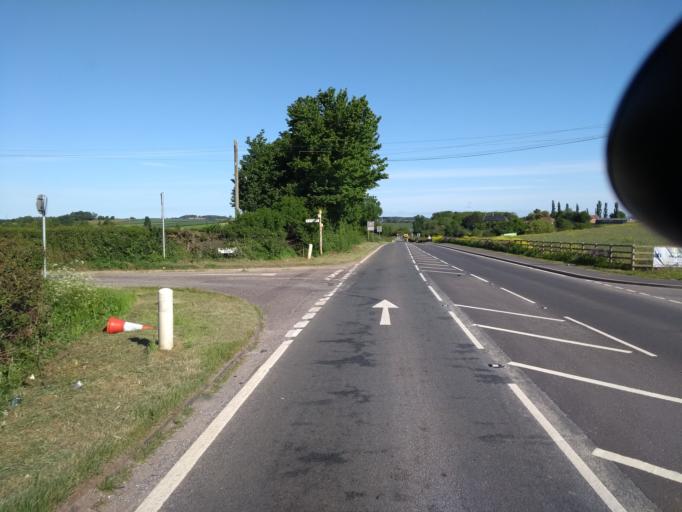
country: GB
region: England
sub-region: Somerset
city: Bridgwater
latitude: 51.1317
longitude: -3.0415
